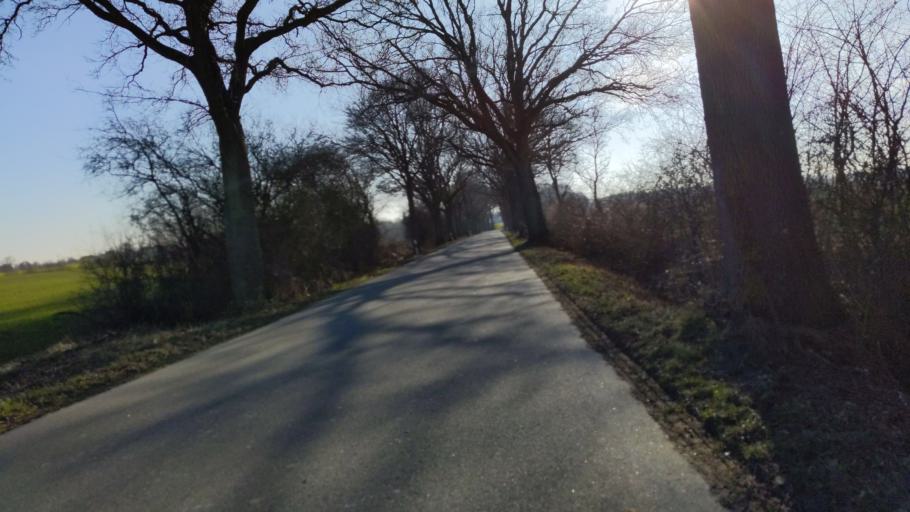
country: DE
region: Schleswig-Holstein
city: Susel
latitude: 54.0220
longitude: 10.6537
